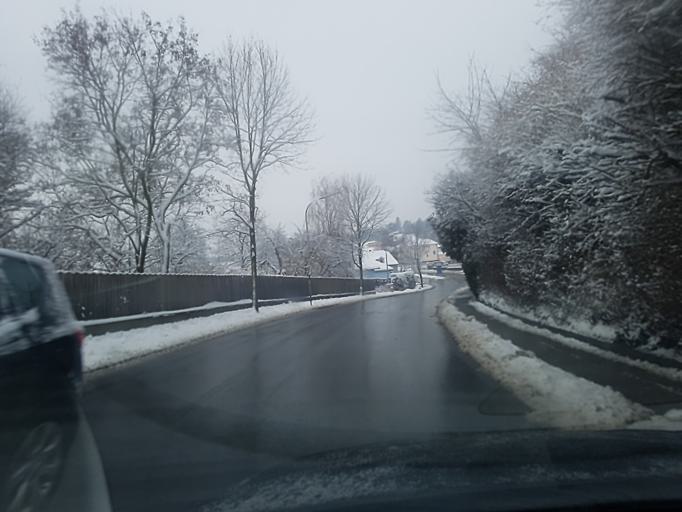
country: AT
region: Burgenland
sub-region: Politischer Bezirk Mattersburg
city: Wiesen
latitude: 47.7726
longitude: 16.3316
